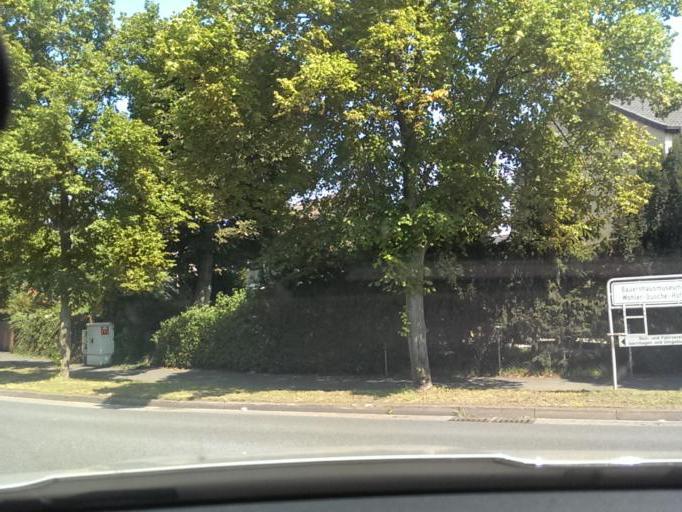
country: DE
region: Lower Saxony
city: Langenhagen
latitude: 52.4547
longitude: 9.7881
